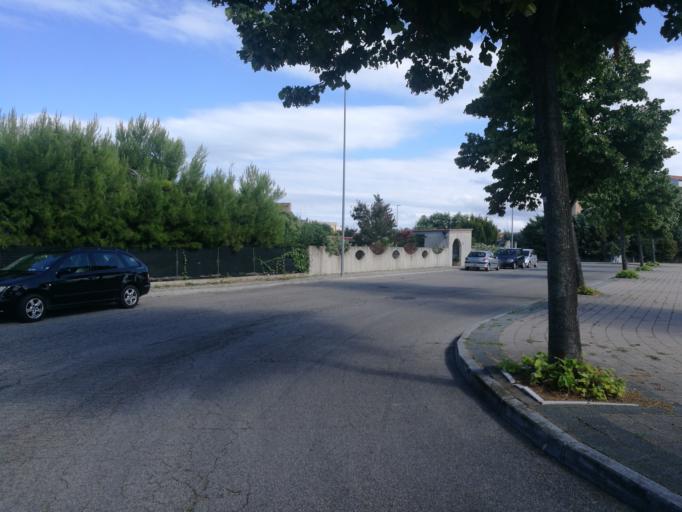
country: IT
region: Molise
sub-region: Provincia di Campobasso
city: Termoli
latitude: 41.9832
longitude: 14.9808
